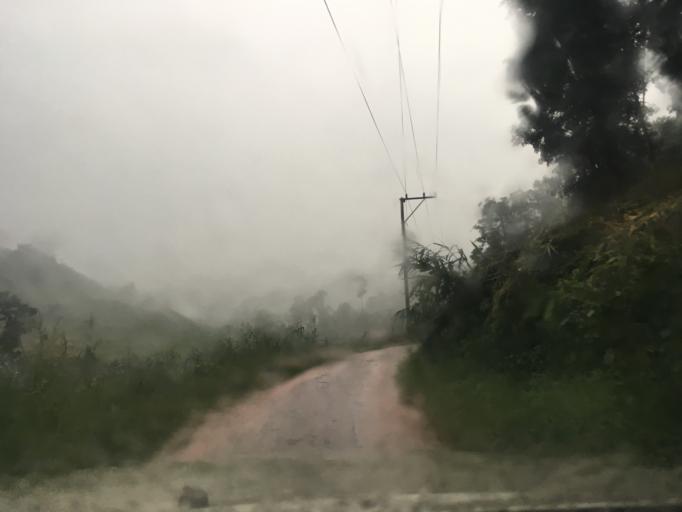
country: LA
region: Oudomxai
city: Muang La
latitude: 21.2313
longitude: 101.9592
